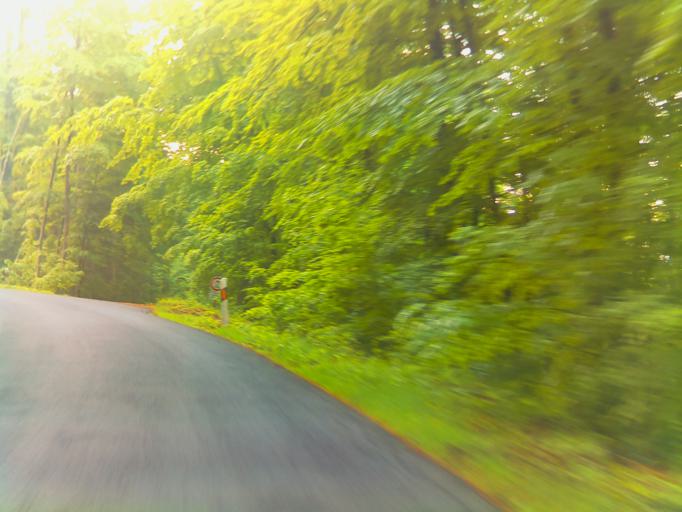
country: DE
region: Bavaria
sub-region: Regierungsbezirk Unterfranken
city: Neuhutten
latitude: 49.9672
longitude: 9.4499
